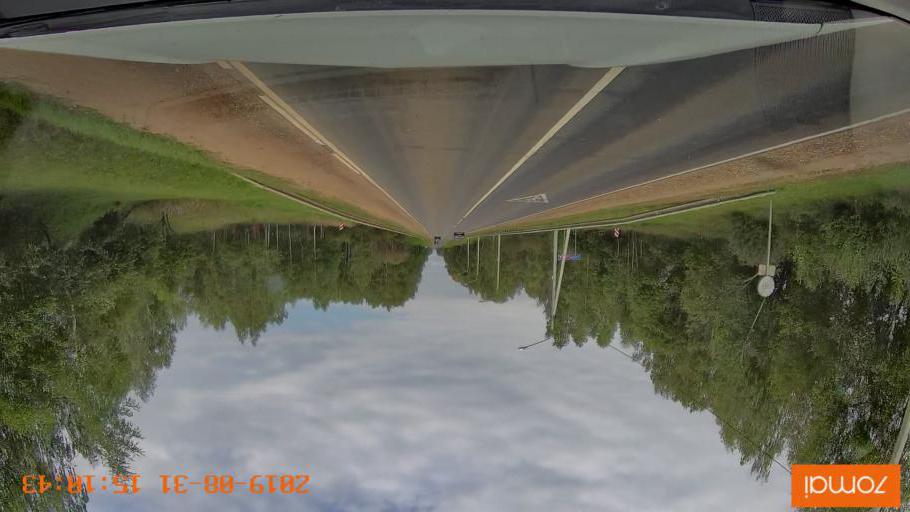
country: RU
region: Kaluga
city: Spas-Demensk
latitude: 54.4165
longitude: 34.2266
